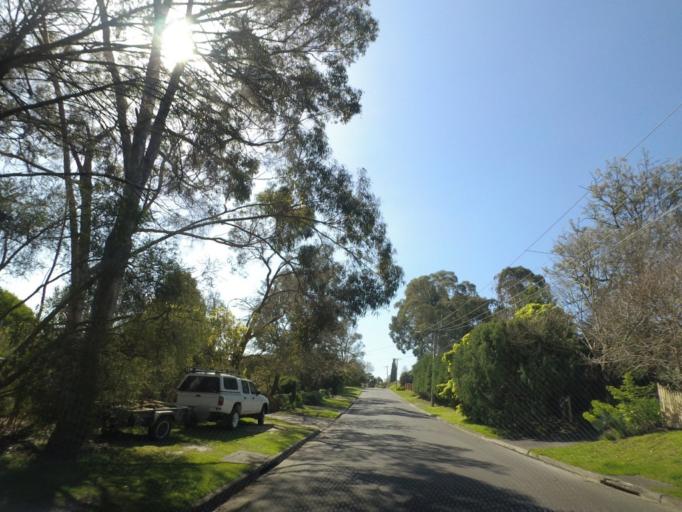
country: AU
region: Victoria
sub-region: Manningham
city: Park Orchards
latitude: -37.7840
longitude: 145.2257
